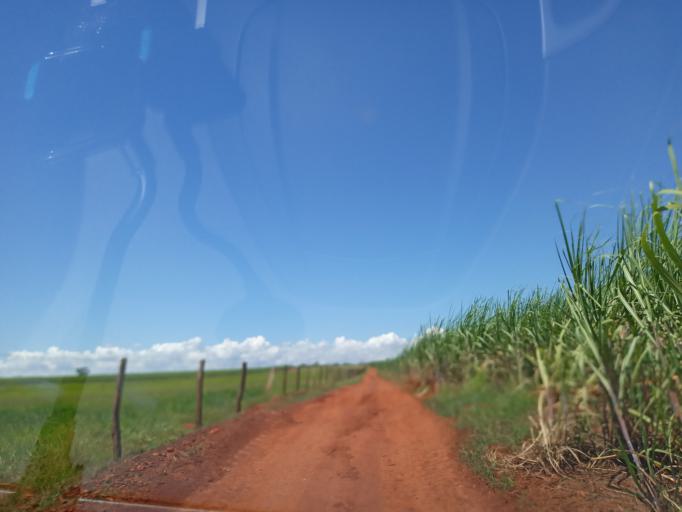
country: BR
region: Goias
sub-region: Itumbiara
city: Itumbiara
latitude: -18.4007
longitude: -49.1305
